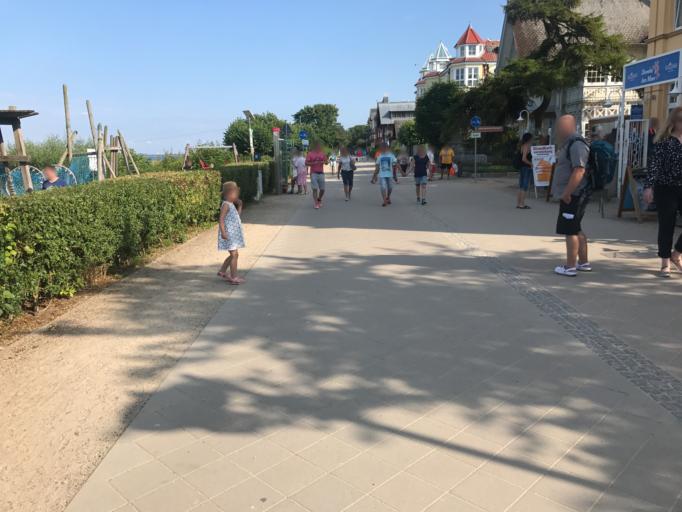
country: DE
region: Mecklenburg-Vorpommern
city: Seebad Bansin
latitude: 53.9717
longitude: 14.1464
